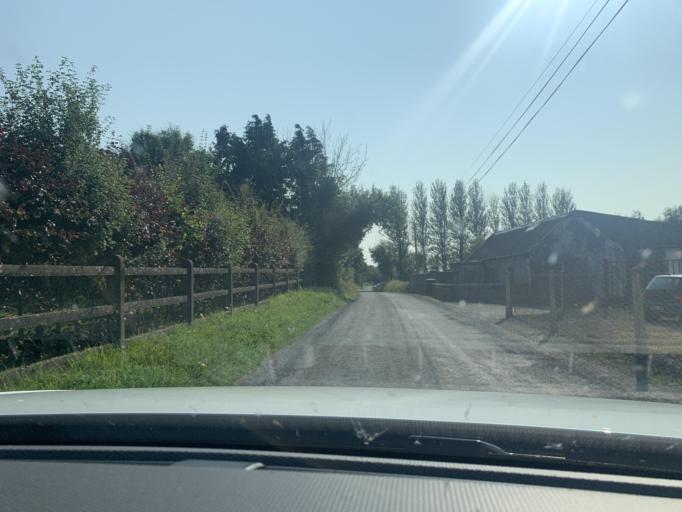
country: IE
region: Connaught
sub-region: Maigh Eo
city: Ballyhaunis
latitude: 53.8126
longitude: -8.7512
